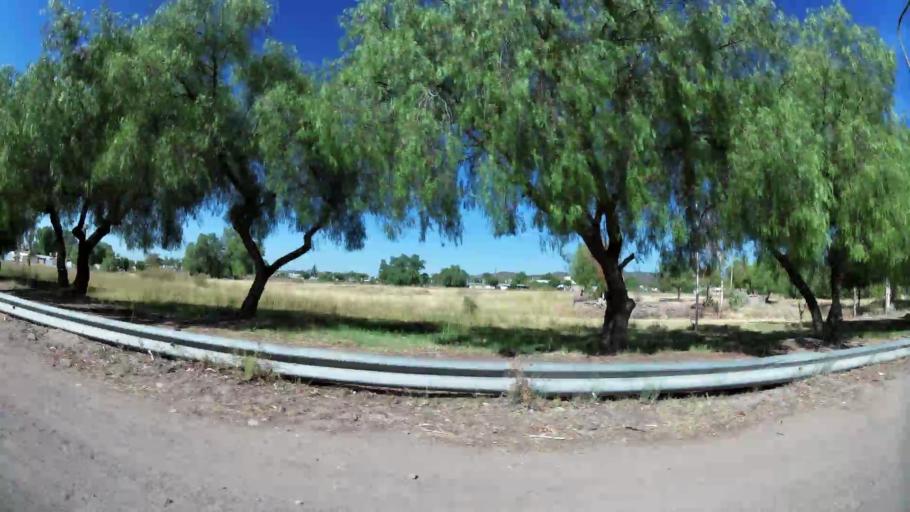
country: AR
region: Mendoza
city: Mendoza
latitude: -32.8989
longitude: -68.8782
